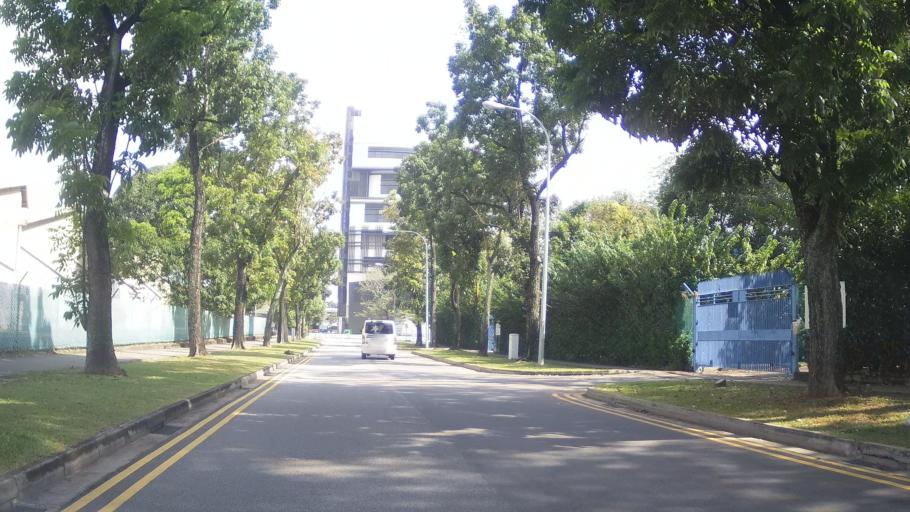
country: MY
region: Johor
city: Johor Bahru
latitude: 1.3265
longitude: 103.7030
